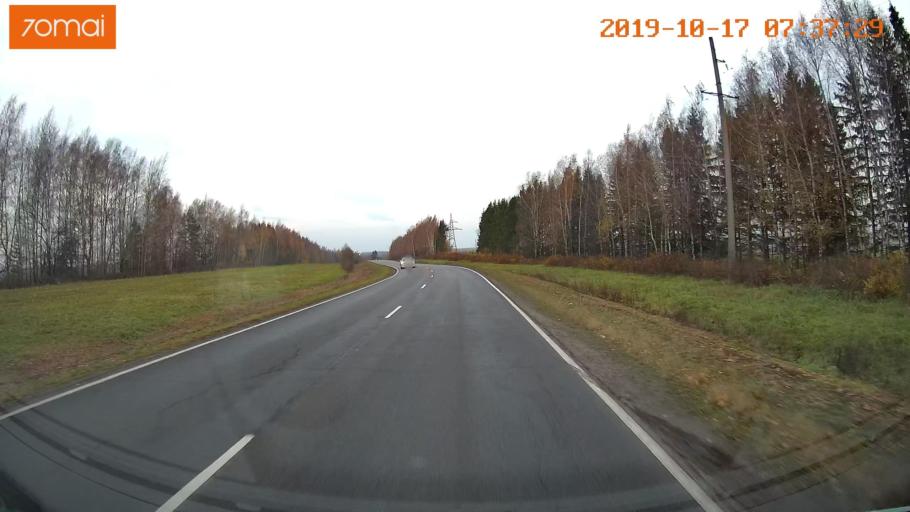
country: RU
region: Vladimir
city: Yur'yev-Pol'skiy
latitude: 56.4497
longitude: 39.8979
